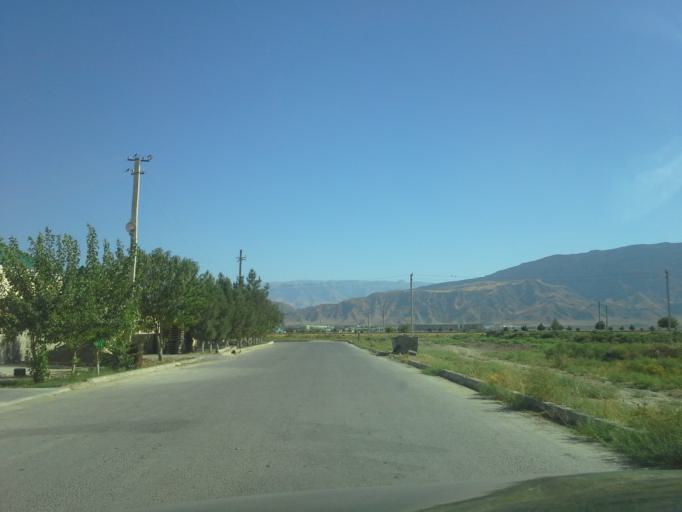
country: TM
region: Ahal
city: Abadan
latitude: 38.0753
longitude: 58.1473
